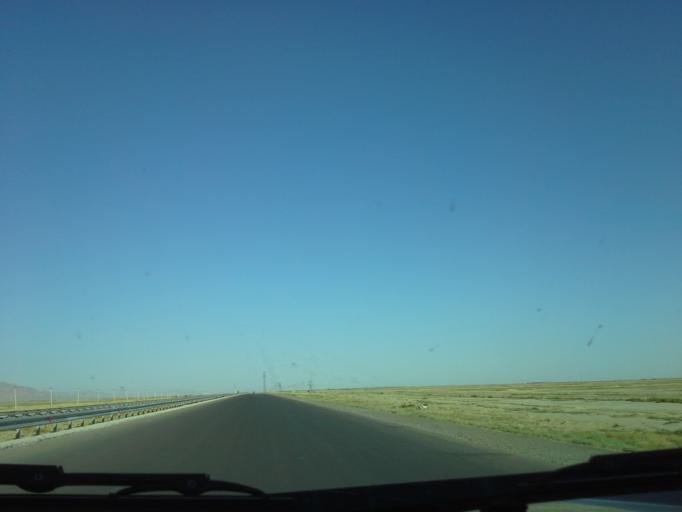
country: TM
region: Balkan
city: Serdar
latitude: 39.0170
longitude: 56.2192
